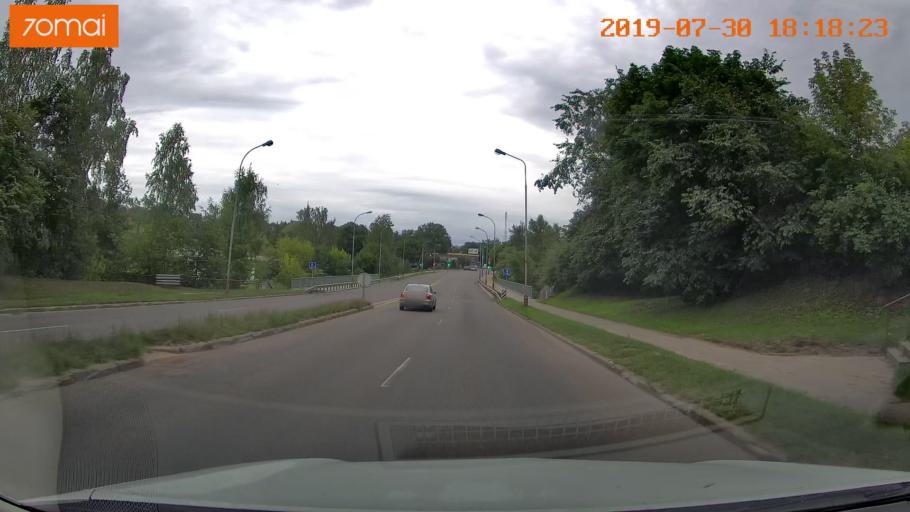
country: LT
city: Skaidiskes
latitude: 54.6893
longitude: 25.4022
